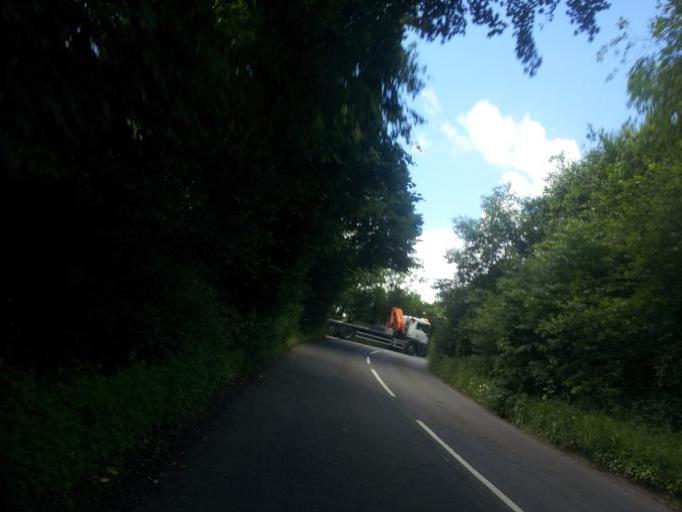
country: GB
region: England
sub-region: Kent
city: West Malling
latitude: 51.3125
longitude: 0.3616
